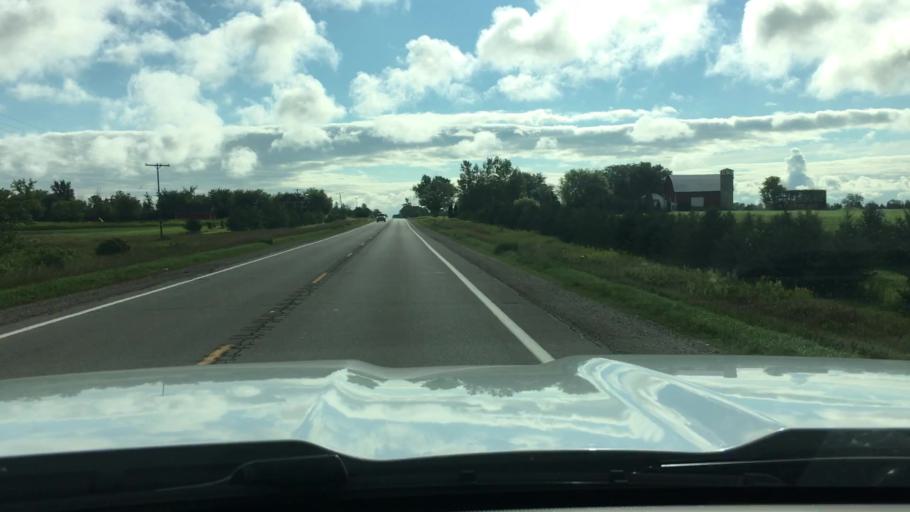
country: US
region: Michigan
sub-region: Tuscola County
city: Cass City
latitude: 43.5994
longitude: -83.2448
